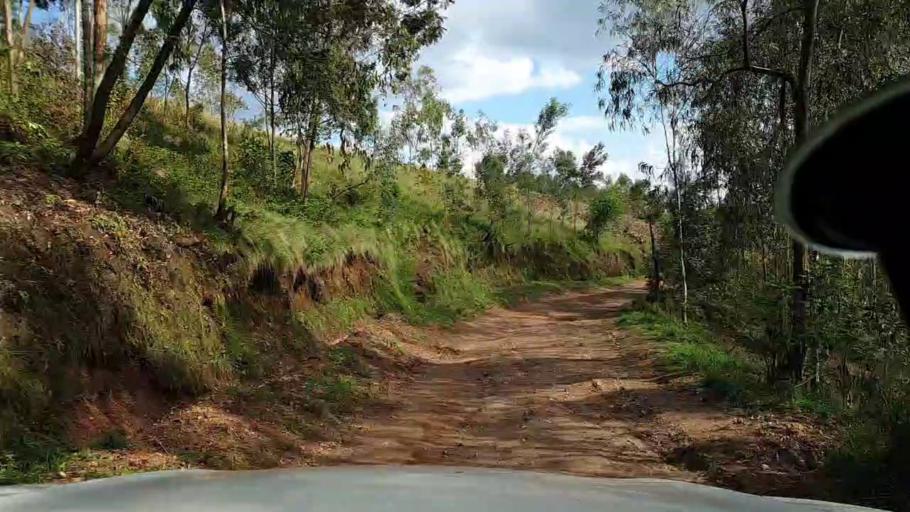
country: RW
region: Kigali
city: Kigali
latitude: -1.7875
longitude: 29.8396
